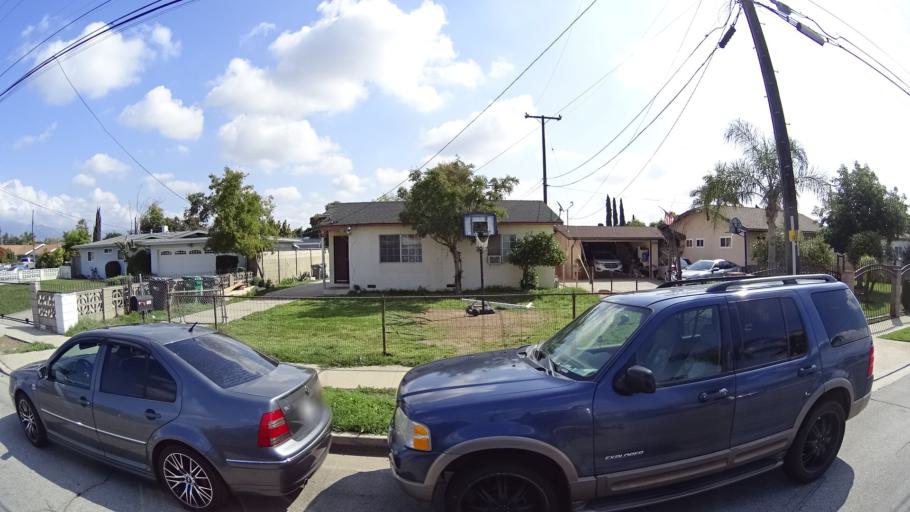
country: US
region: California
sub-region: Los Angeles County
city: Baldwin Park
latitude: 34.0788
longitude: -117.9802
